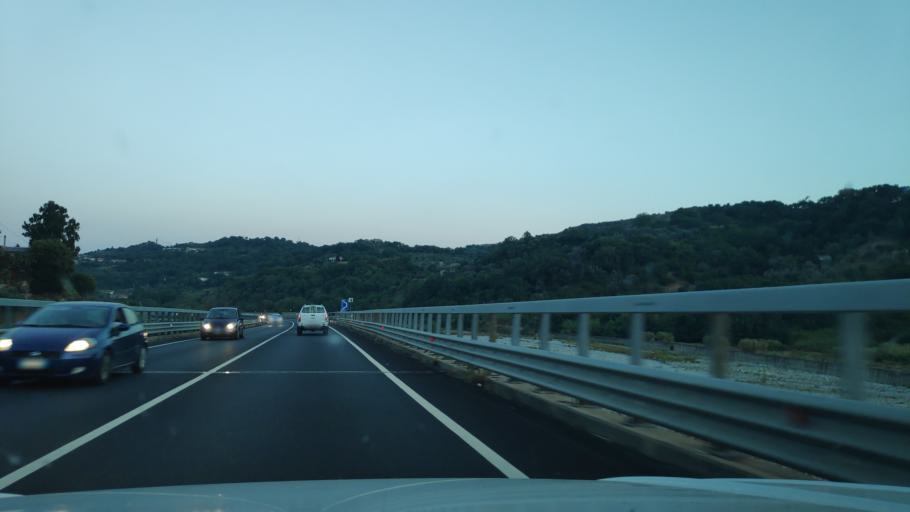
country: IT
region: Calabria
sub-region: Provincia di Reggio Calabria
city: Grotteria
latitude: 38.3475
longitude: 16.2565
